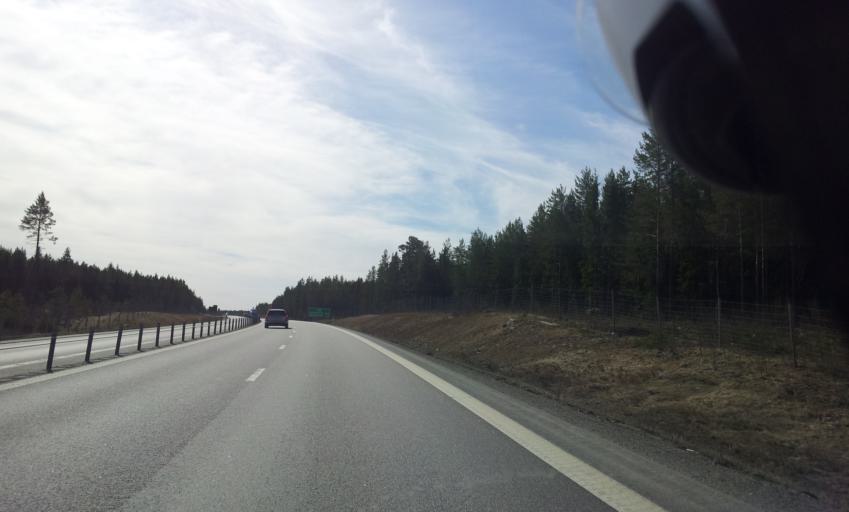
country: SE
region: Gaevleborg
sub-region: Hudiksvalls Kommun
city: Hudiksvall
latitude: 61.7101
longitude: 17.0486
